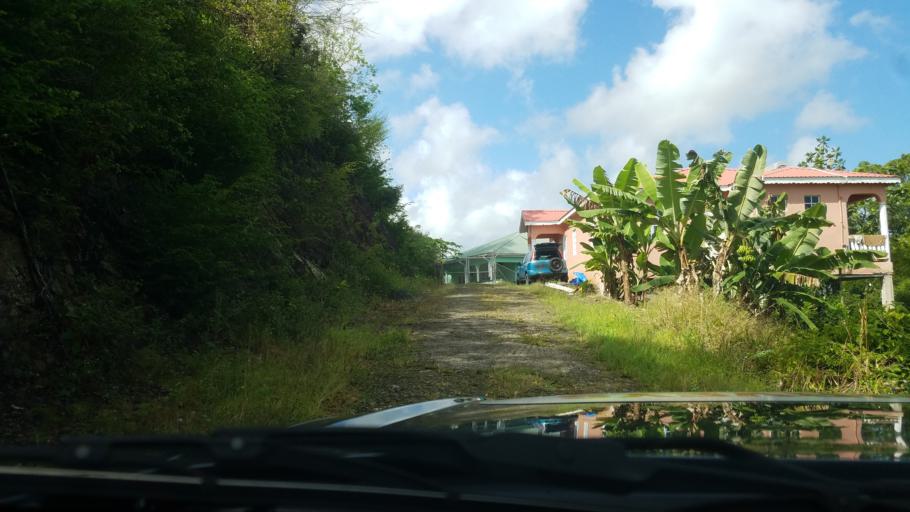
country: LC
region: Castries Quarter
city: Bisee
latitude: 14.0197
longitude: -60.9769
